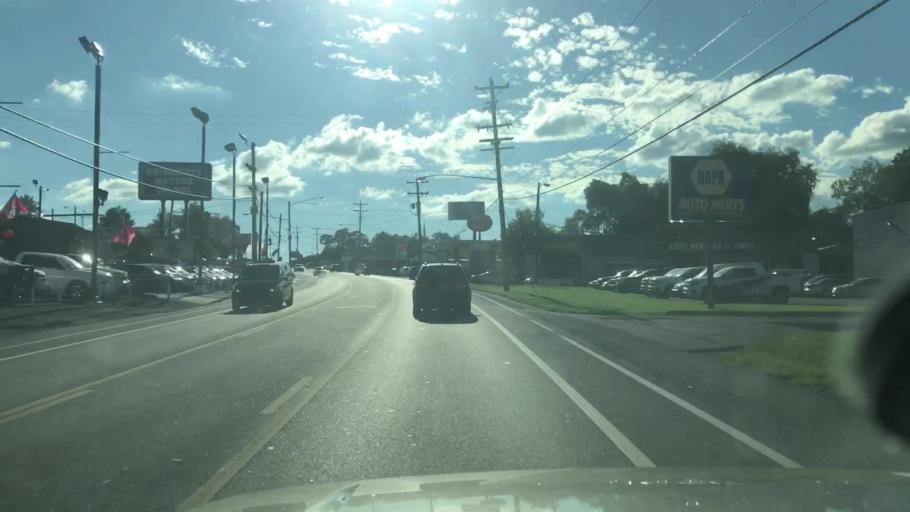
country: US
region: Tennessee
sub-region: Davidson County
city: Belle Meade
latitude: 36.1487
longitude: -86.8654
